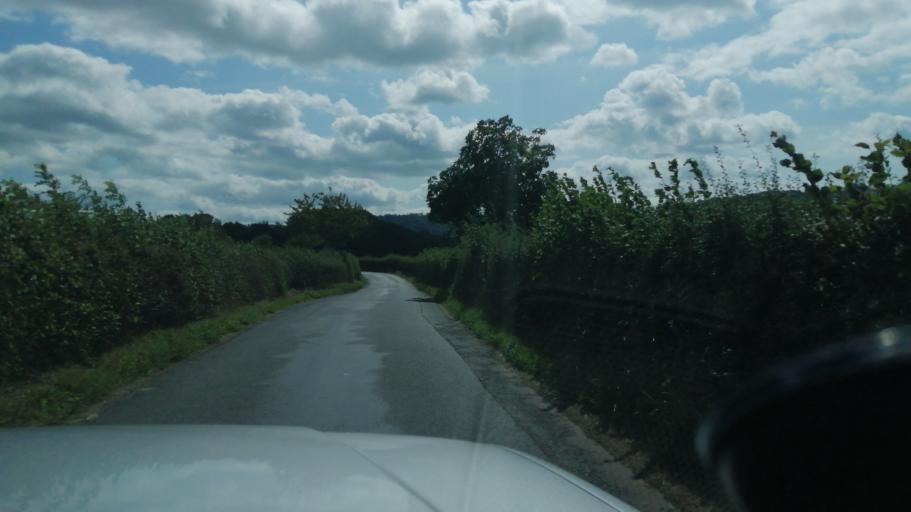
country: GB
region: England
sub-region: Herefordshire
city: Kinnersley
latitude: 52.1069
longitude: -2.9651
